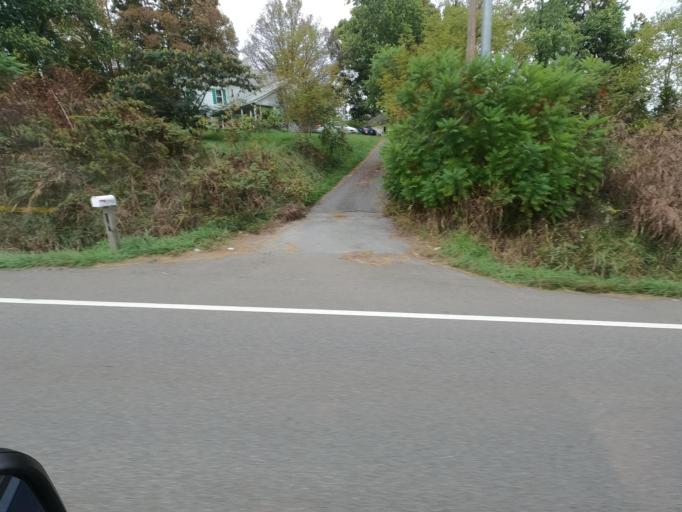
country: US
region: Tennessee
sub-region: Washington County
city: Midway
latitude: 36.3097
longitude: -82.4377
